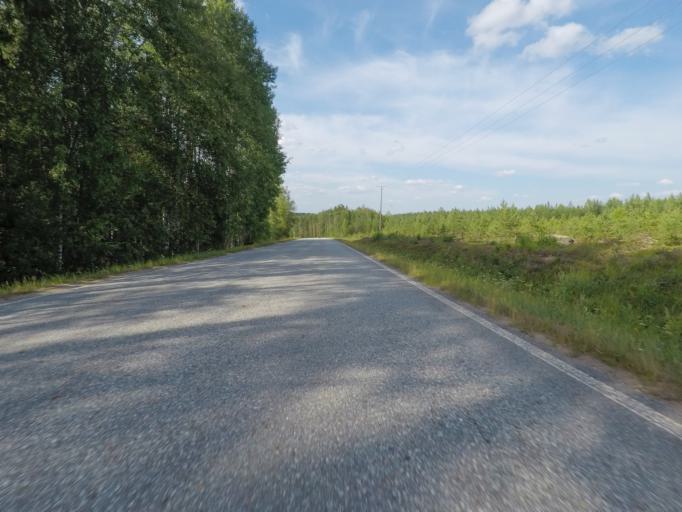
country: FI
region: Southern Savonia
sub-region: Savonlinna
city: Sulkava
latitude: 61.7152
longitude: 28.2101
